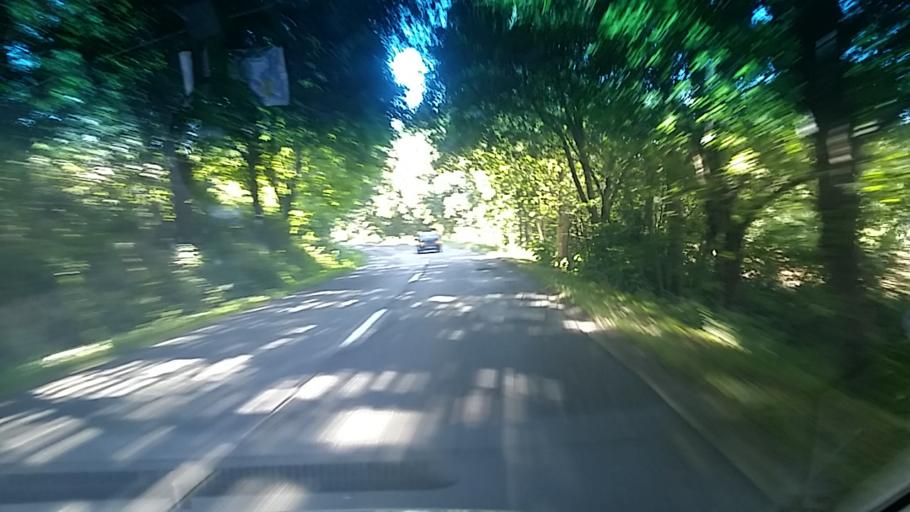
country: HU
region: Nograd
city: Retsag
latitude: 47.9370
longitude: 19.1548
